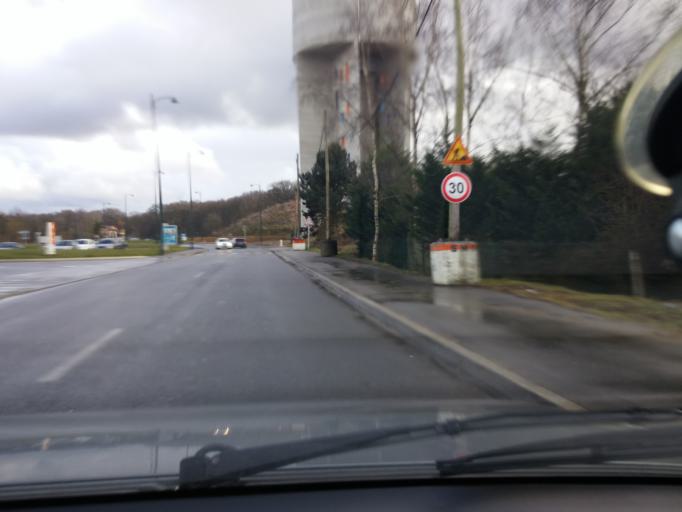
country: FR
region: Ile-de-France
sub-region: Departement du Val-de-Marne
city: La Queue-en-Brie
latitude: 48.7748
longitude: 2.5932
